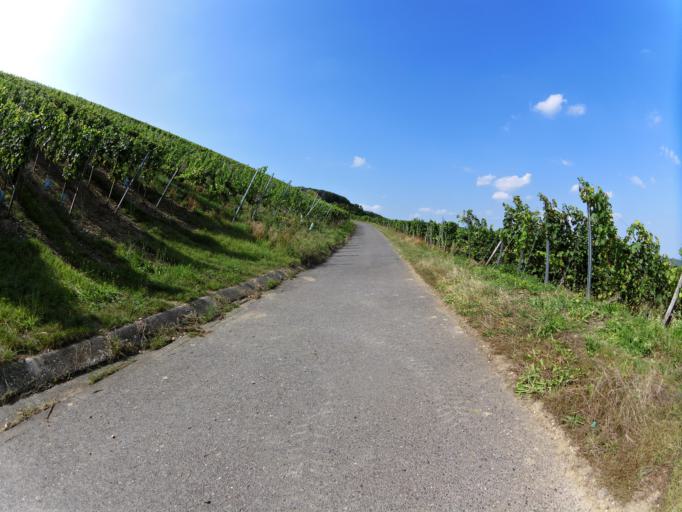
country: DE
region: Bavaria
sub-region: Regierungsbezirk Unterfranken
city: Nordheim
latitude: 49.8381
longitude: 10.1731
